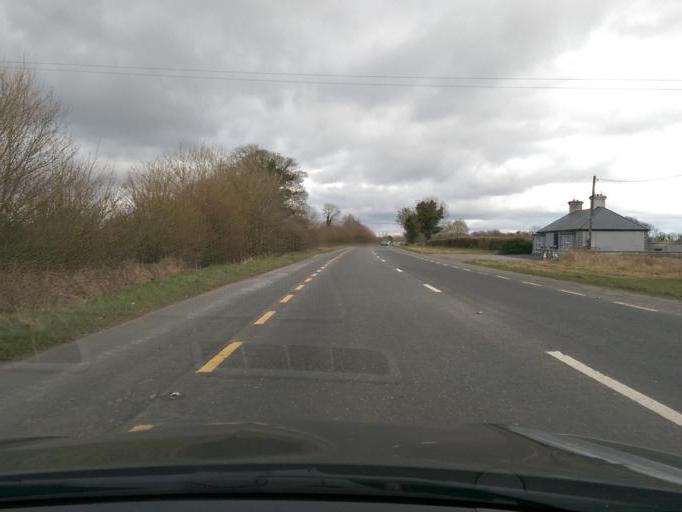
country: IE
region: Leinster
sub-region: An Iarmhi
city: Moate
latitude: 53.3917
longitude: -7.7966
